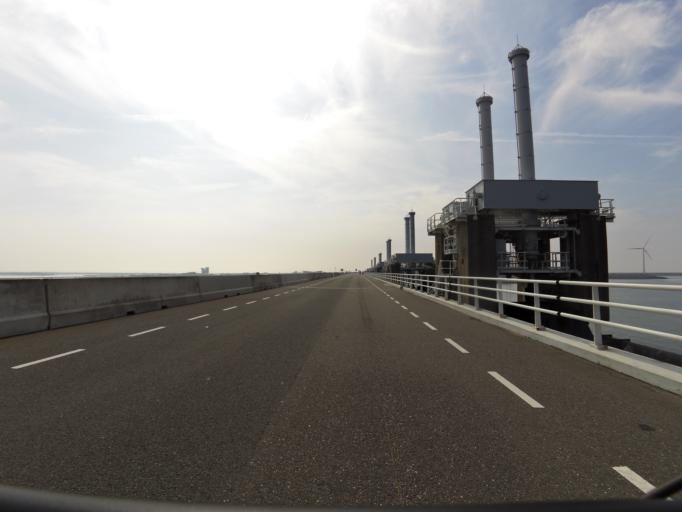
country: NL
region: Zeeland
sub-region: Schouwen-Duiveland
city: Burgh
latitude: 51.6450
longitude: 3.7163
